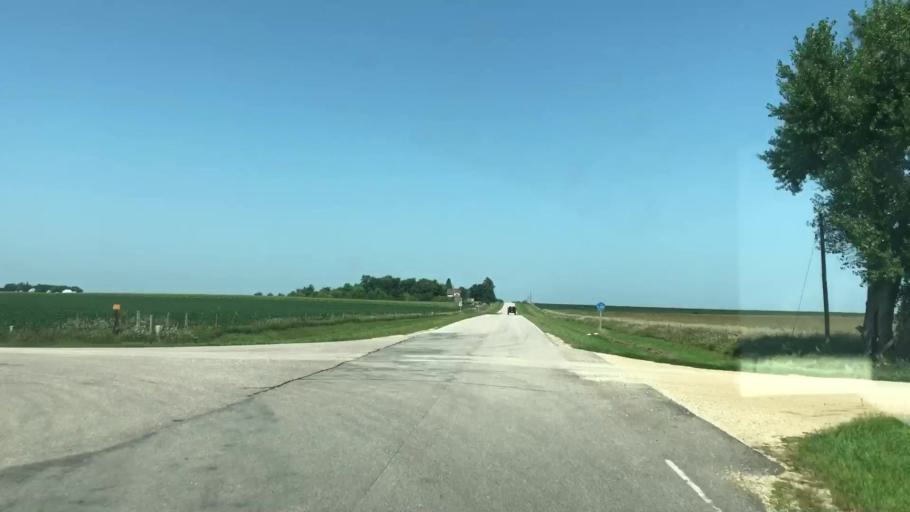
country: US
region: Iowa
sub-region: O'Brien County
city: Sanborn
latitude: 43.2440
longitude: -95.7234
